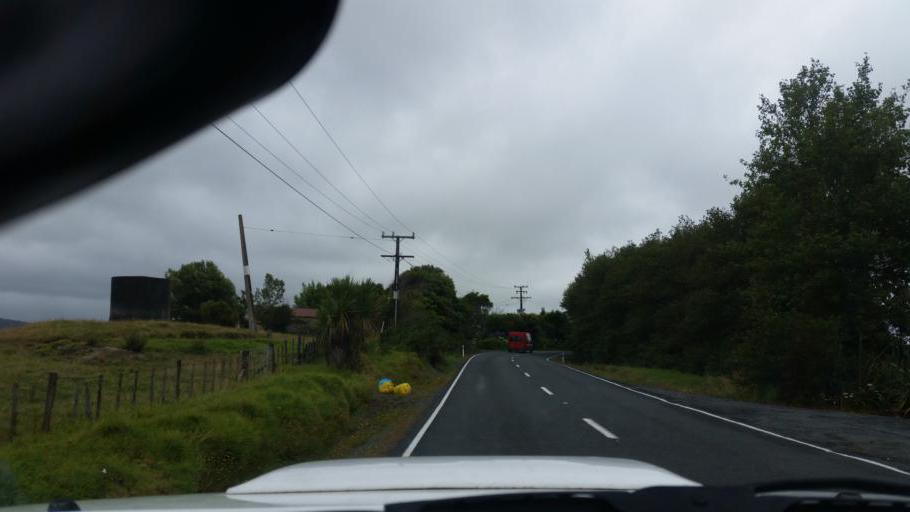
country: NZ
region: Auckland
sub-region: Auckland
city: Wellsford
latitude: -36.1475
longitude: 174.4763
